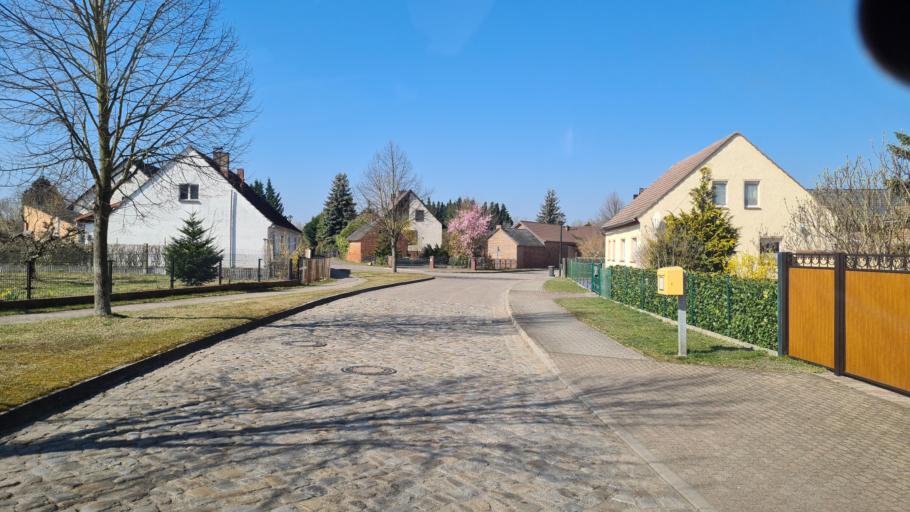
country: DE
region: Brandenburg
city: Calau
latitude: 51.7993
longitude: 13.9694
